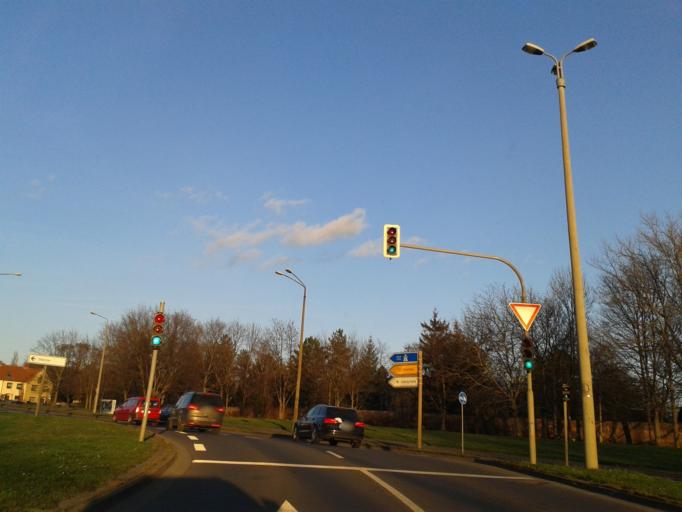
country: DE
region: Saxony-Anhalt
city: Halle (Saale)
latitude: 51.4917
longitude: 11.9816
